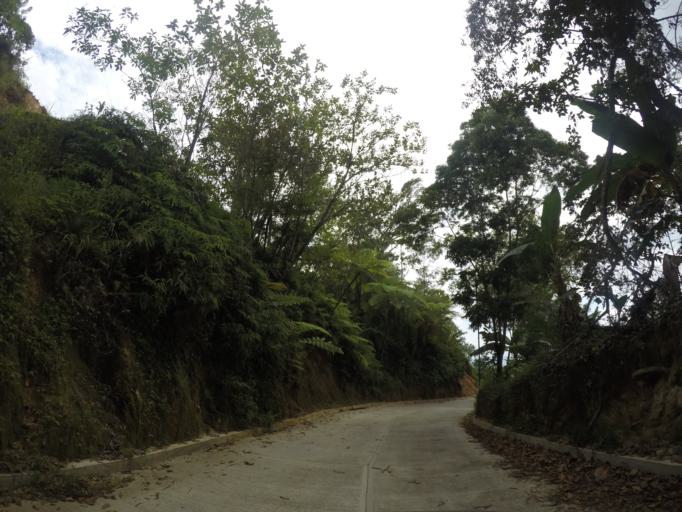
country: MX
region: Oaxaca
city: Pluma Hidalgo
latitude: 15.9155
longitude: -96.4164
